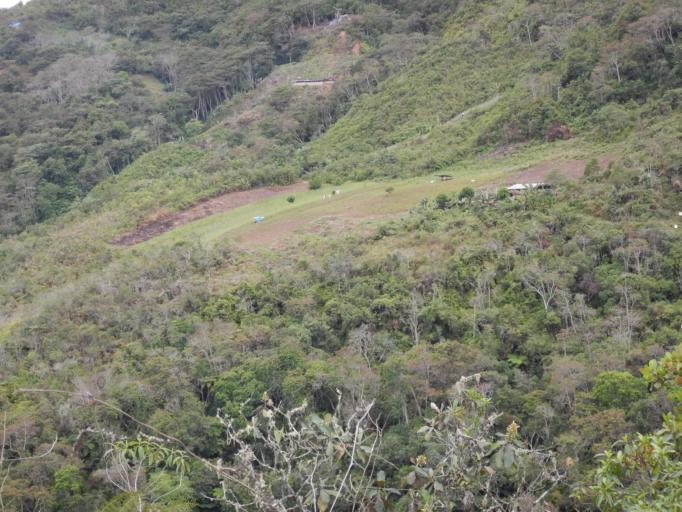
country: BO
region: La Paz
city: Coroico
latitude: -16.1262
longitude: -67.7626
